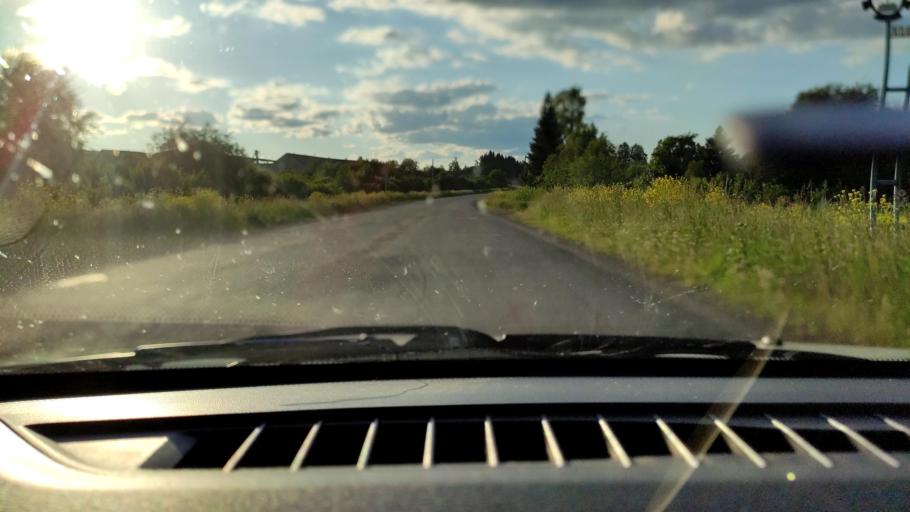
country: RU
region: Perm
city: Uinskoye
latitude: 57.1046
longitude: 56.5355
